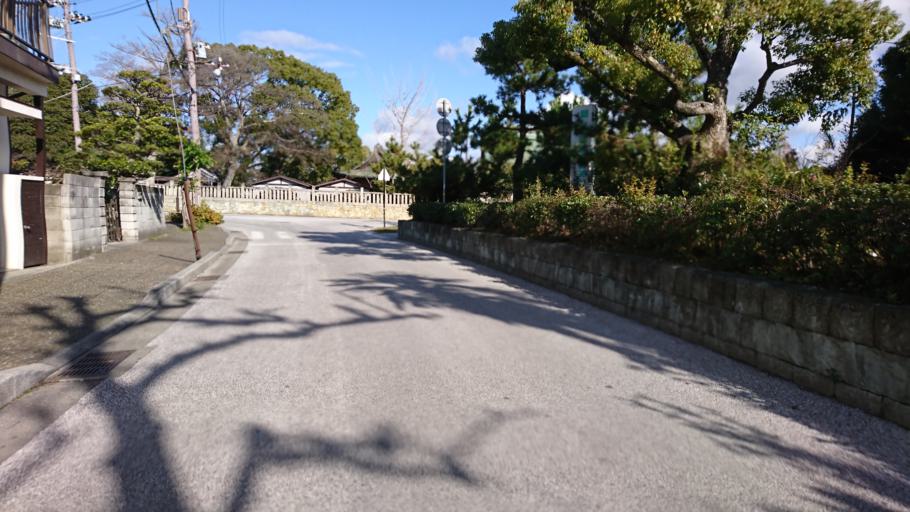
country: JP
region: Hyogo
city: Shirahamacho-usazakiminami
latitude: 34.7769
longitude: 134.7728
